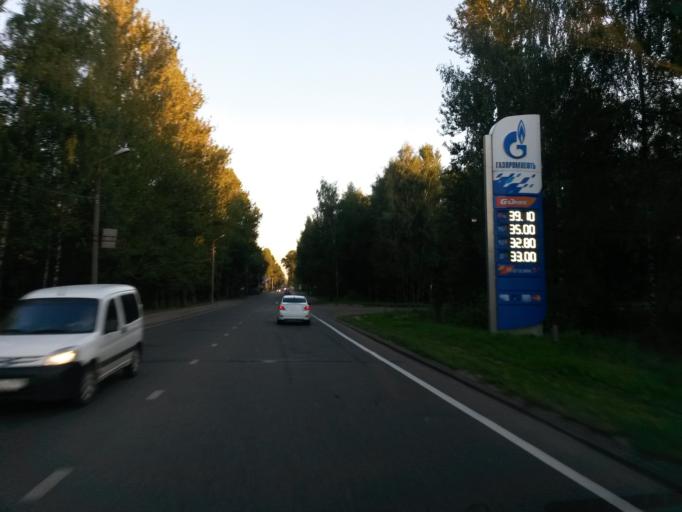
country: RU
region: Jaroslavl
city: Yaroslavl
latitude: 57.6673
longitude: 39.9087
